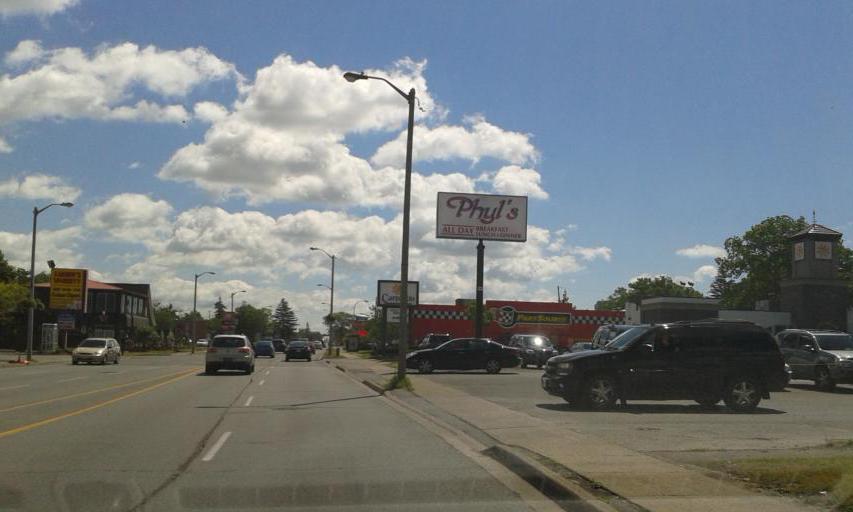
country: CA
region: Ontario
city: Niagara Falls
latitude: 43.0892
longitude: -79.1104
